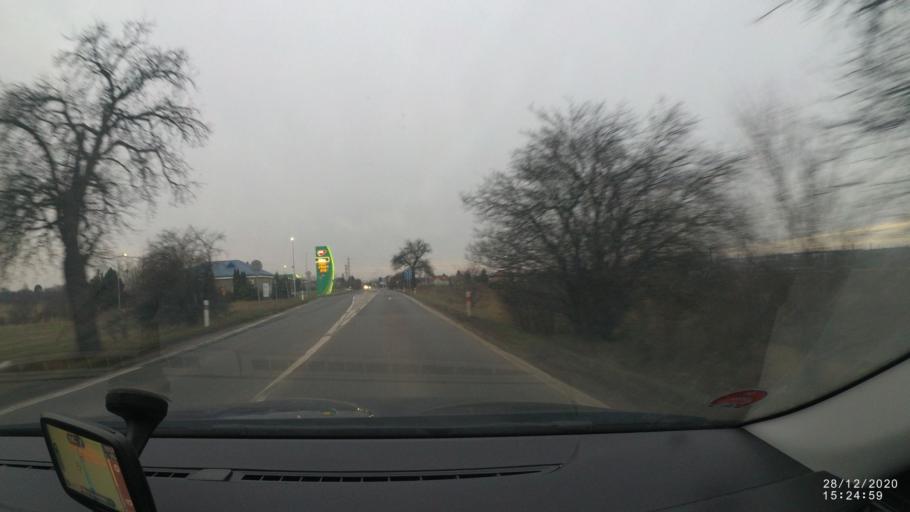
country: CZ
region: Praha
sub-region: Praha 20
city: Horni Pocernice
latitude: 50.0801
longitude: 14.6306
